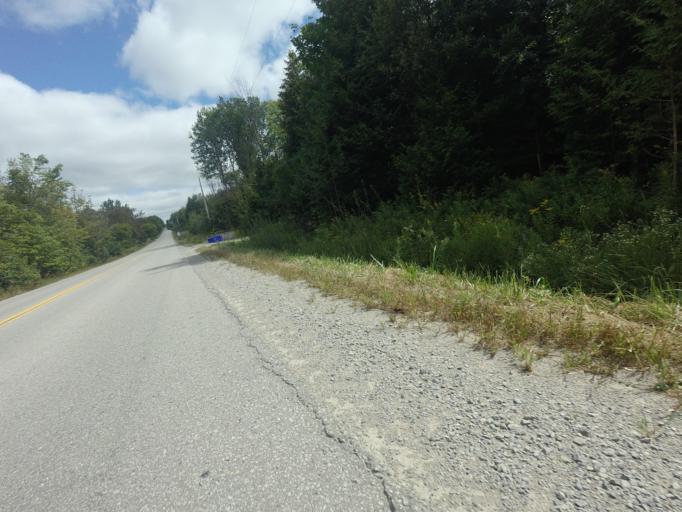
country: CA
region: Ontario
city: Uxbridge
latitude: 44.1235
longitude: -79.1755
